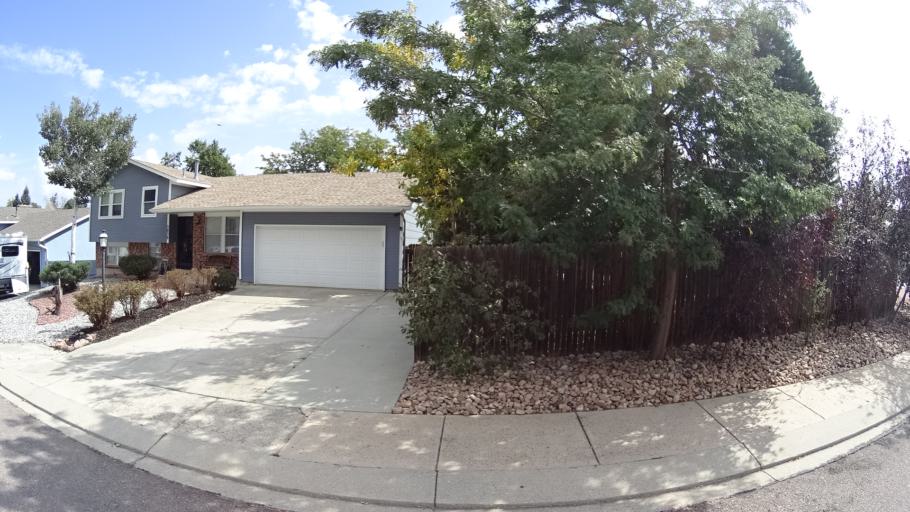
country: US
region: Colorado
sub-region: El Paso County
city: Cimarron Hills
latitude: 38.8627
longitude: -104.7609
